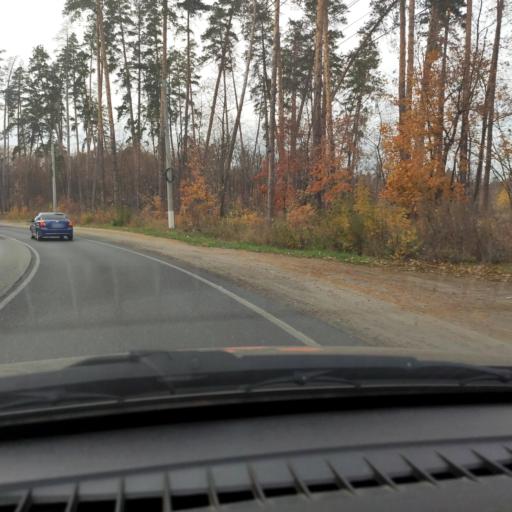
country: RU
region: Samara
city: Tol'yatti
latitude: 53.4914
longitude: 49.3054
